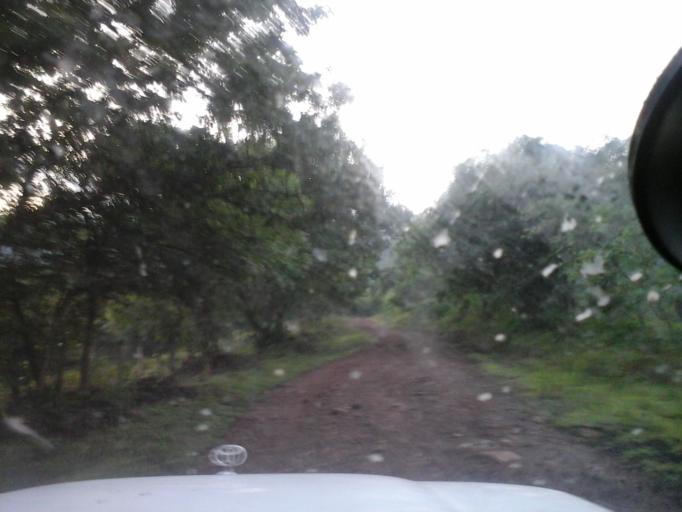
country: CO
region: Cesar
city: Agustin Codazzi
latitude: 10.1717
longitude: -73.1656
